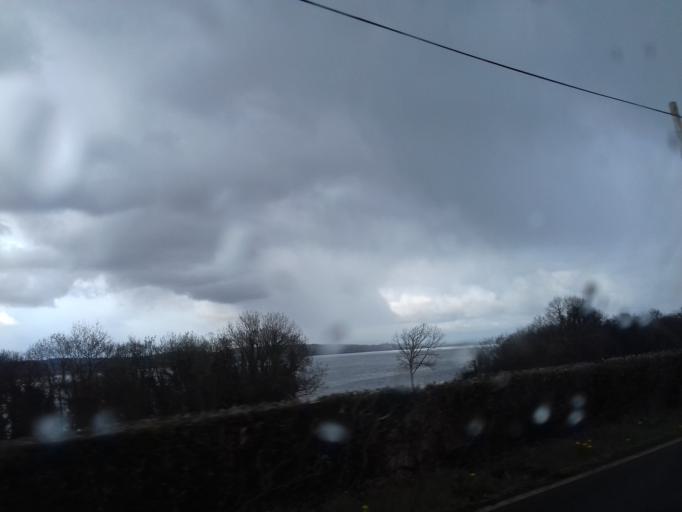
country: IE
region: Ulster
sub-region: County Donegal
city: Ballyshannon
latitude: 54.4735
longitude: -7.9473
